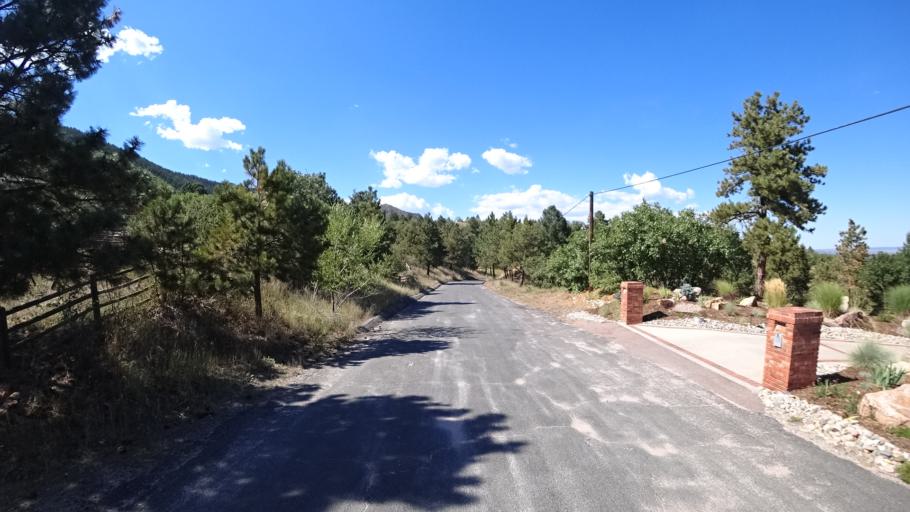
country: US
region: Colorado
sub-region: El Paso County
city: Colorado Springs
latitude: 38.8132
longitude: -104.8759
